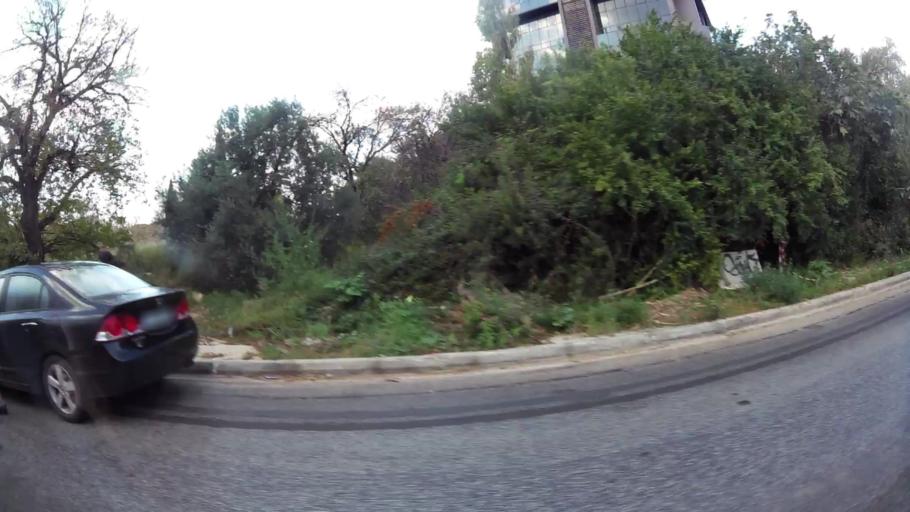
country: GR
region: Attica
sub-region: Nomarchia Athinas
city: Marousi
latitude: 38.0467
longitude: 23.8095
